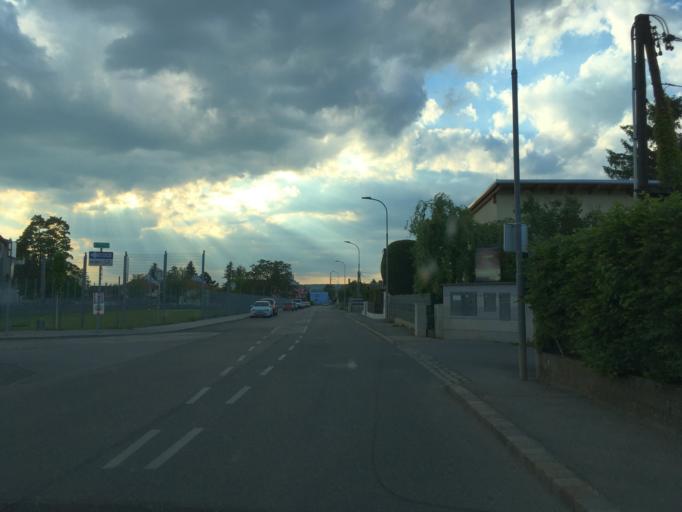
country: AT
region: Lower Austria
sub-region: Politischer Bezirk Wien-Umgebung
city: Gerasdorf bei Wien
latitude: 48.2865
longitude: 16.4519
